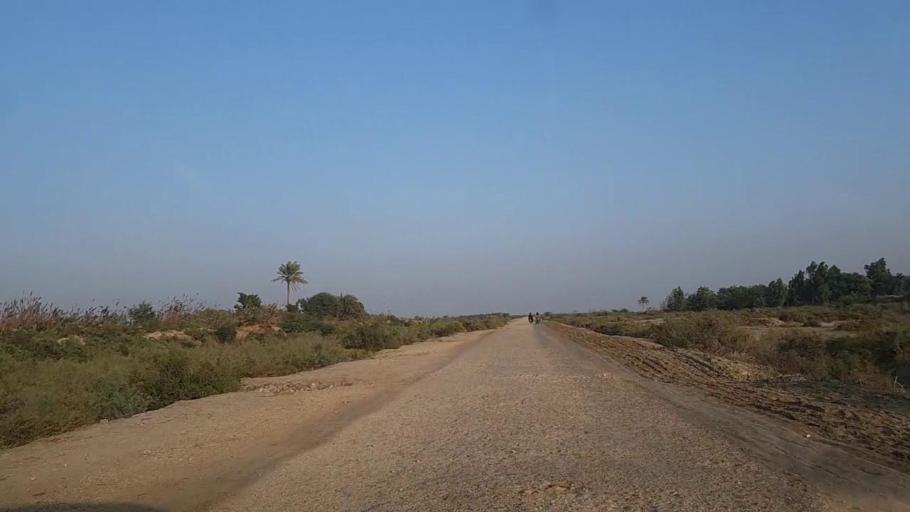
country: PK
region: Sindh
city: Keti Bandar
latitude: 24.2718
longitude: 67.6784
